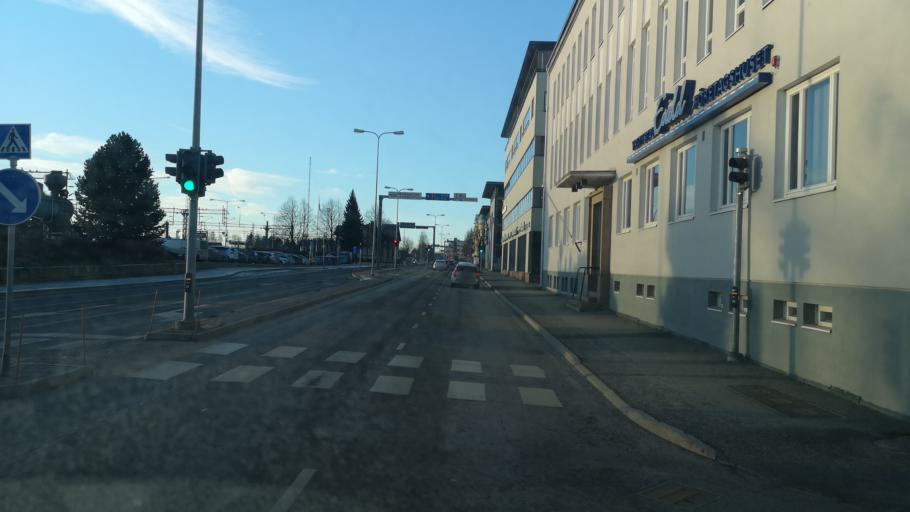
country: FI
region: Central Ostrobothnia
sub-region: Kokkola
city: Kokkola
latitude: 63.8353
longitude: 23.1352
